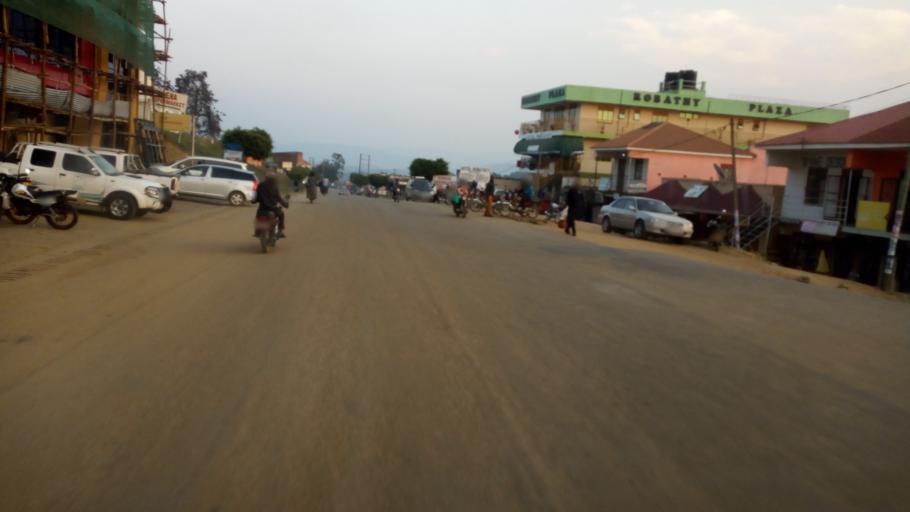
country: UG
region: Western Region
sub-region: Rukungiri District
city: Rukungiri
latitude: -0.7878
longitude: 29.9263
